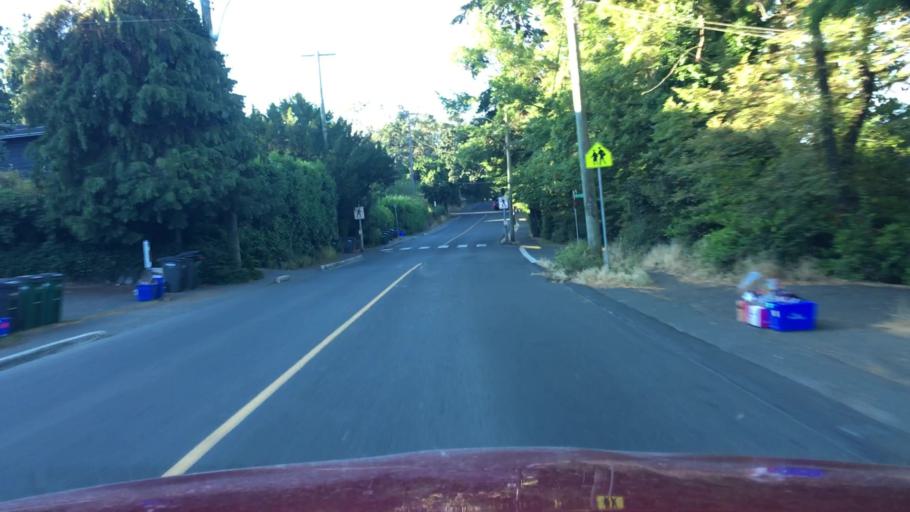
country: CA
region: British Columbia
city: Oak Bay
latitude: 48.4532
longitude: -123.3267
